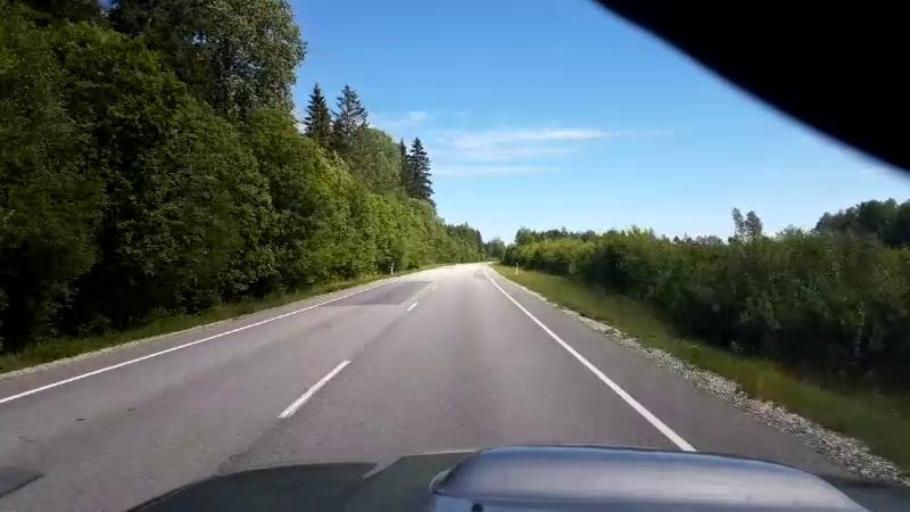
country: EE
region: Jaervamaa
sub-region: Koeru vald
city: Koeru
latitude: 58.9739
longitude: 26.1213
